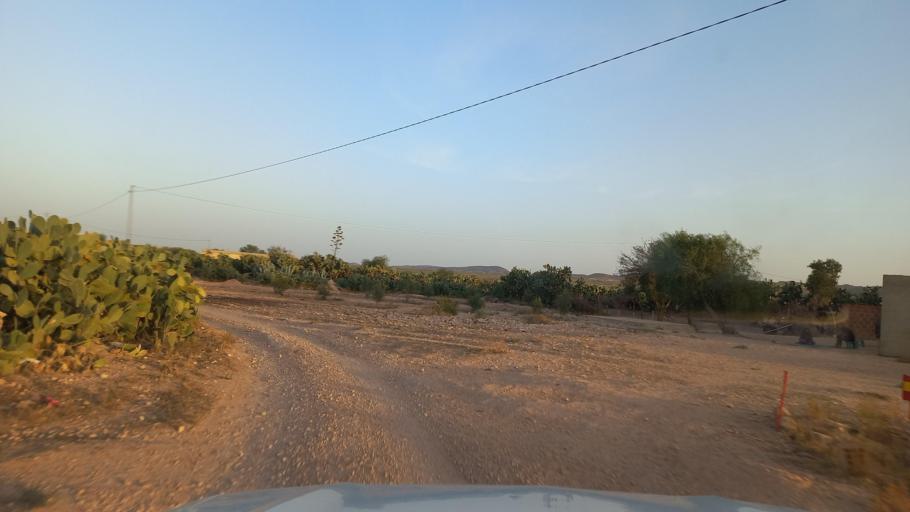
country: TN
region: Al Qasrayn
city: Kasserine
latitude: 35.2401
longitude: 8.9915
